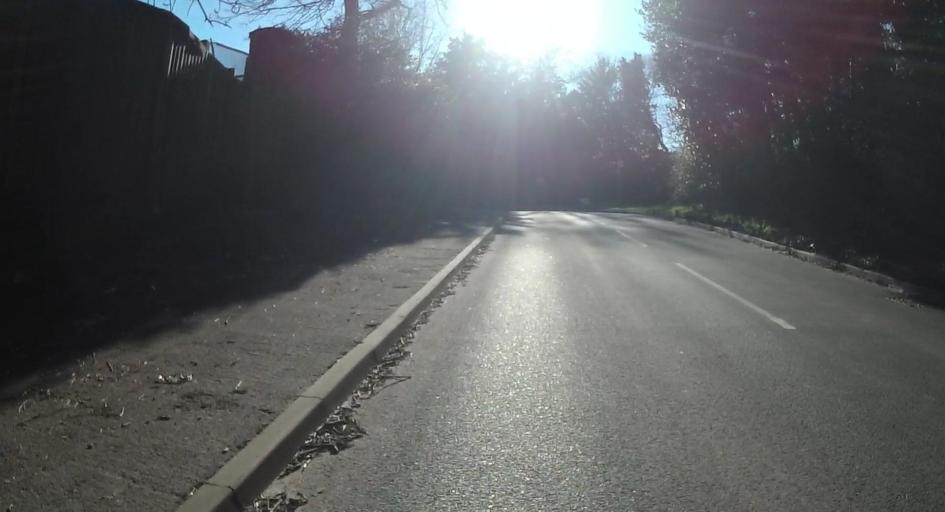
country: GB
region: England
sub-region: Surrey
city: Knaphill
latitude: 51.3209
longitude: -0.6219
